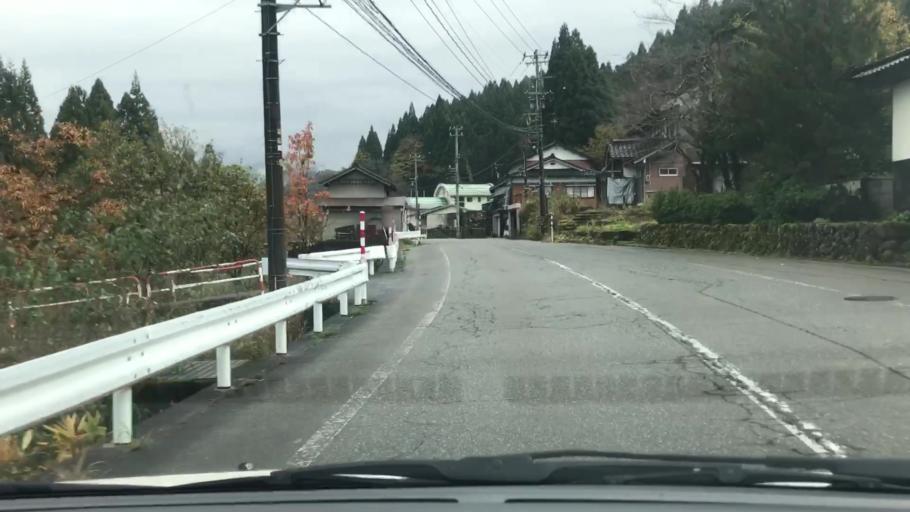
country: JP
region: Toyama
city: Kamiichi
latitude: 36.5700
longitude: 137.3526
